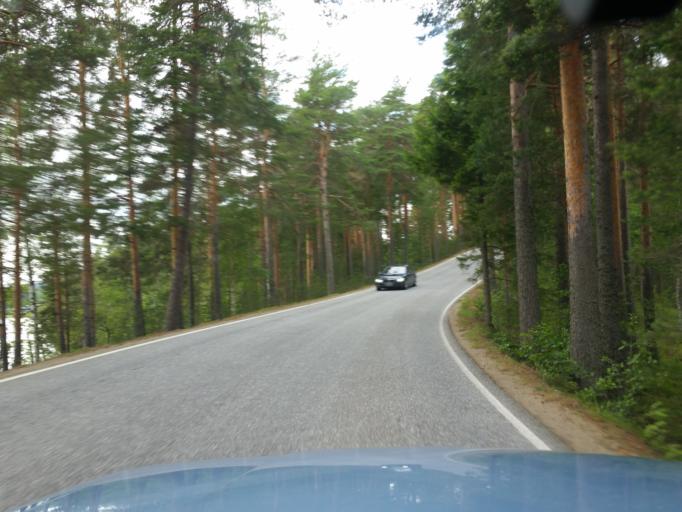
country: FI
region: Southern Savonia
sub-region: Savonlinna
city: Sulkava
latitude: 61.7740
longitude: 28.4298
